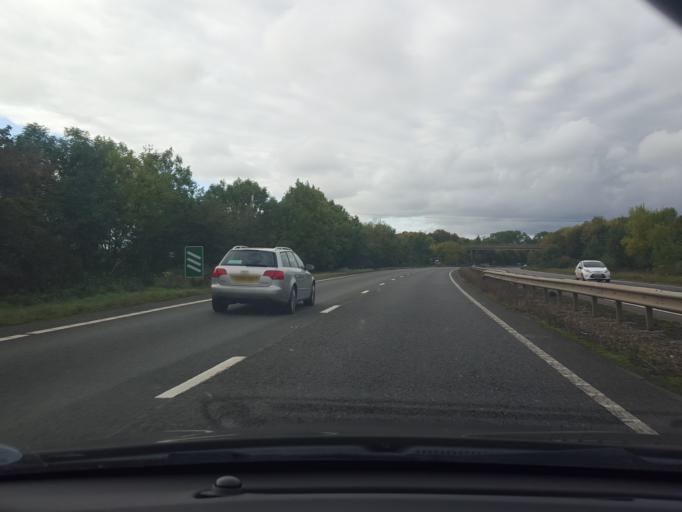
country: GB
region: England
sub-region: Suffolk
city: Woolpit
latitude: 52.2298
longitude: 0.8529
